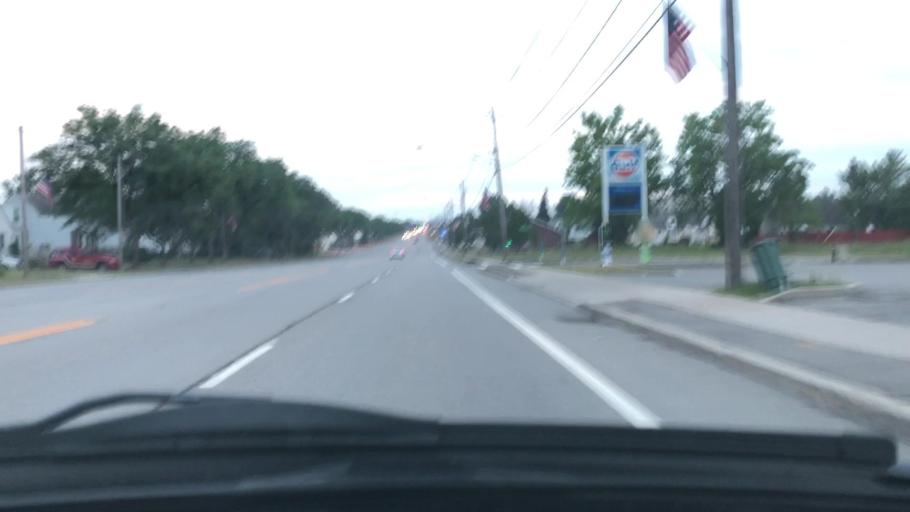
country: US
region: New York
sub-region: Erie County
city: Sloan
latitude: 42.9100
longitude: -78.7842
